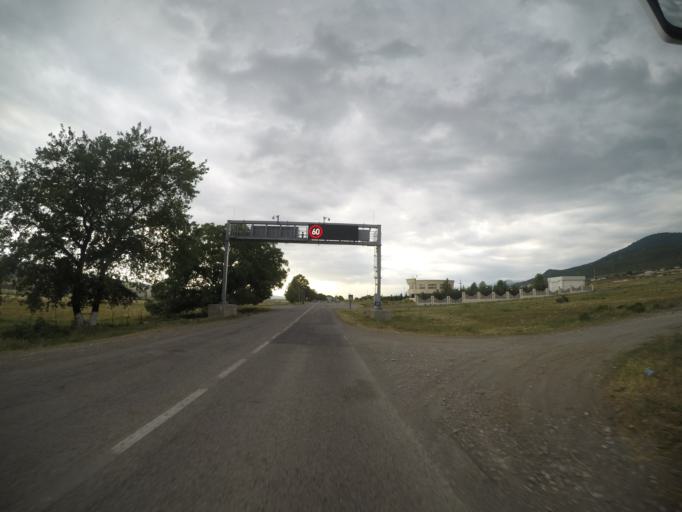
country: AZ
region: Ismayilli
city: Ismayilli
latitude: 40.7569
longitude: 48.2221
